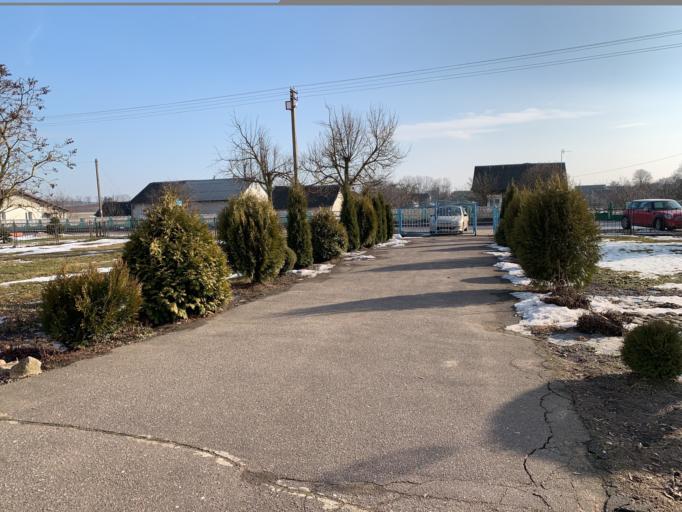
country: BY
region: Minsk
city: Snow
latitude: 53.2195
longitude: 26.4085
